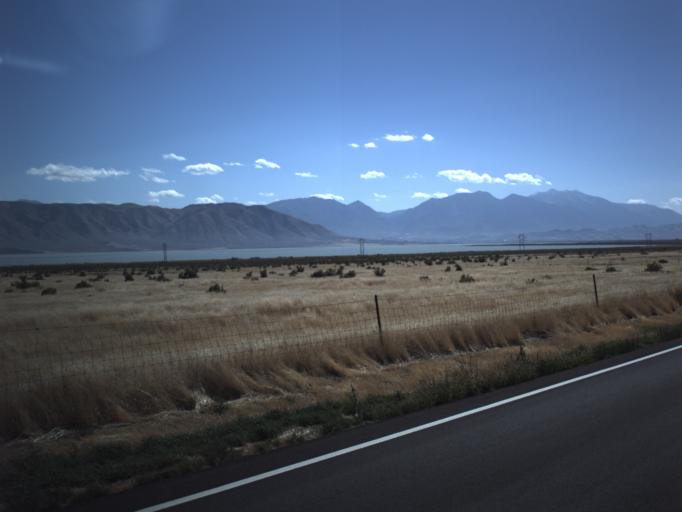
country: US
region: Utah
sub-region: Utah County
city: Eagle Mountain
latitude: 40.1508
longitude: -111.9496
